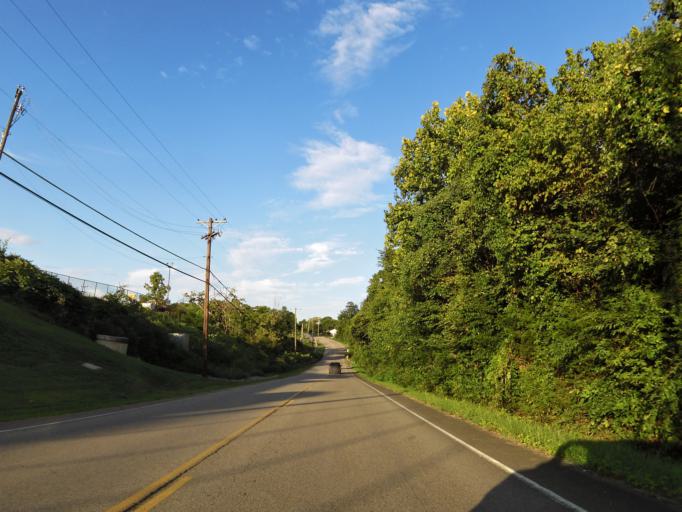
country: US
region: Tennessee
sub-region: Knox County
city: Mascot
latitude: 36.0282
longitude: -83.8369
